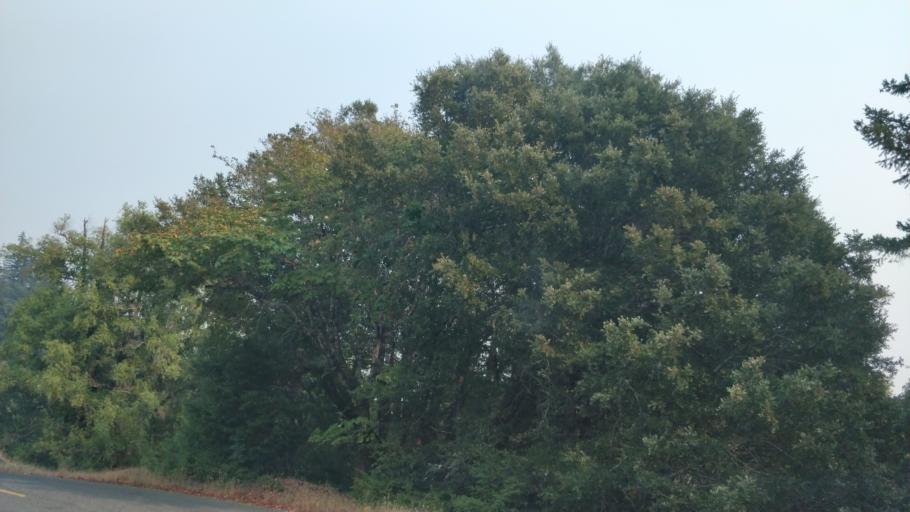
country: US
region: California
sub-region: Humboldt County
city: Rio Dell
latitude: 40.2471
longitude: -124.1212
